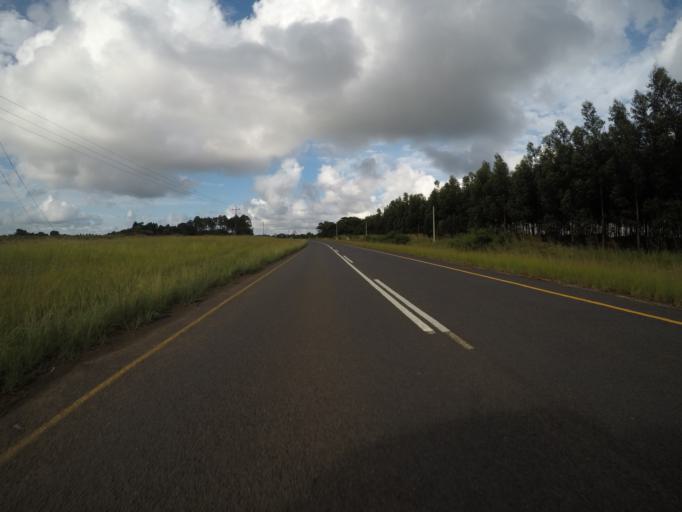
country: ZA
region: KwaZulu-Natal
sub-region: uMkhanyakude District Municipality
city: Mtubatuba
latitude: -28.3799
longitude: 32.2474
